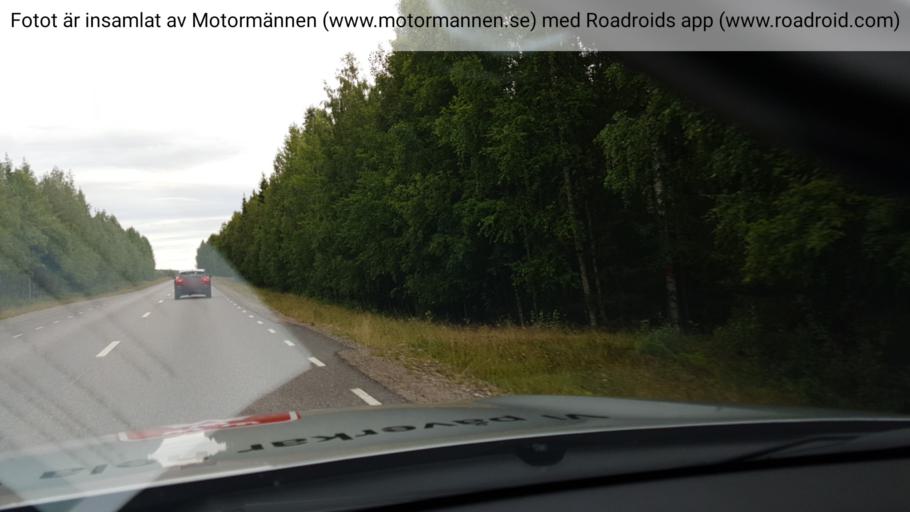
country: SE
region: Norrbotten
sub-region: Overkalix Kommun
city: OEverkalix
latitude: 66.5776
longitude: 22.7585
